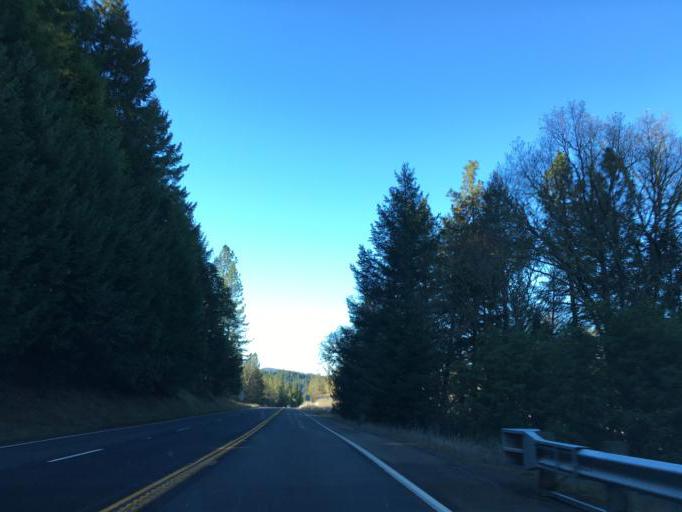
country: US
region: California
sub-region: Mendocino County
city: Laytonville
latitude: 39.7116
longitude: -123.4929
